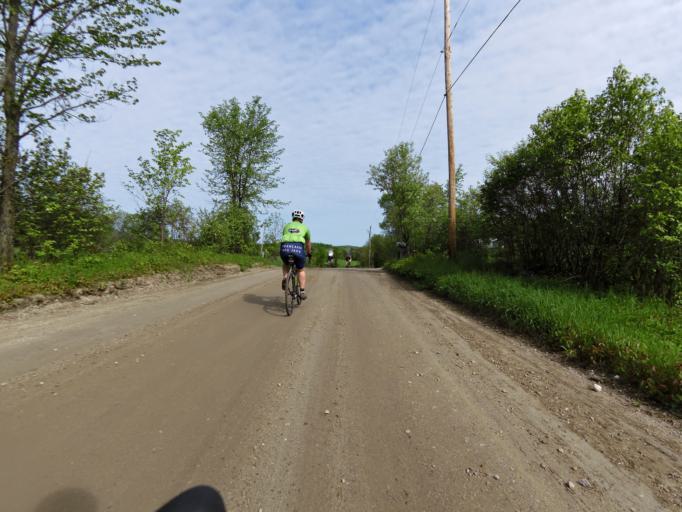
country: CA
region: Quebec
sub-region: Outaouais
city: Wakefield
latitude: 45.7027
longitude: -75.8968
